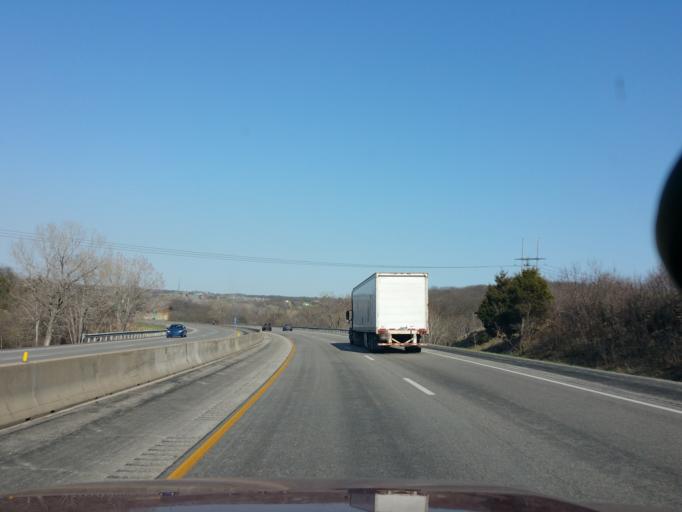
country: US
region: Kansas
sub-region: Wyandotte County
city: Bonner Springs
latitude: 39.0844
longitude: -94.9311
